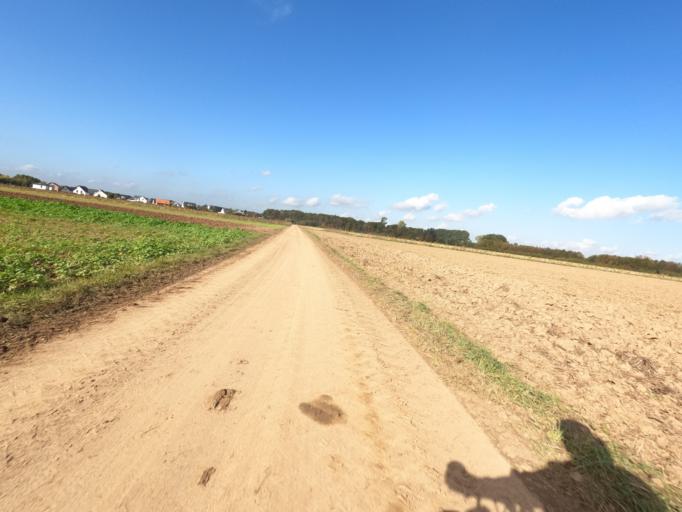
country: DE
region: North Rhine-Westphalia
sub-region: Regierungsbezirk Koln
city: Inden
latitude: 50.8706
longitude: 6.4086
